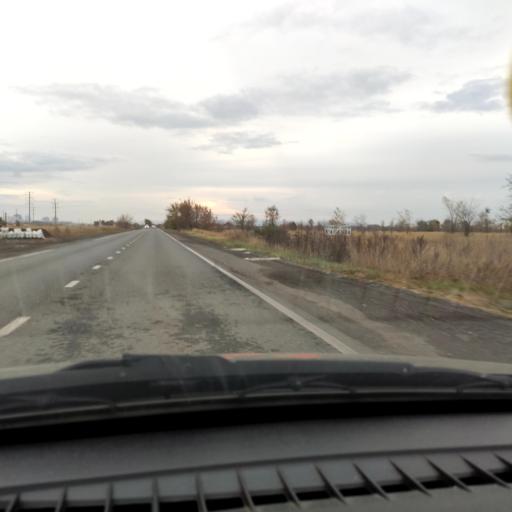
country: RU
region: Samara
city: Podstepki
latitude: 53.5213
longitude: 49.2018
